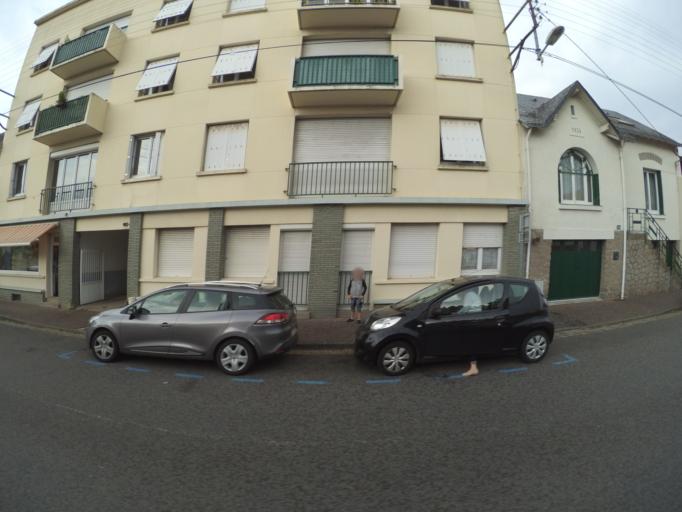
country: FR
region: Pays de la Loire
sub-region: Departement de la Loire-Atlantique
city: Reze
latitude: 47.1860
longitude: -1.5271
